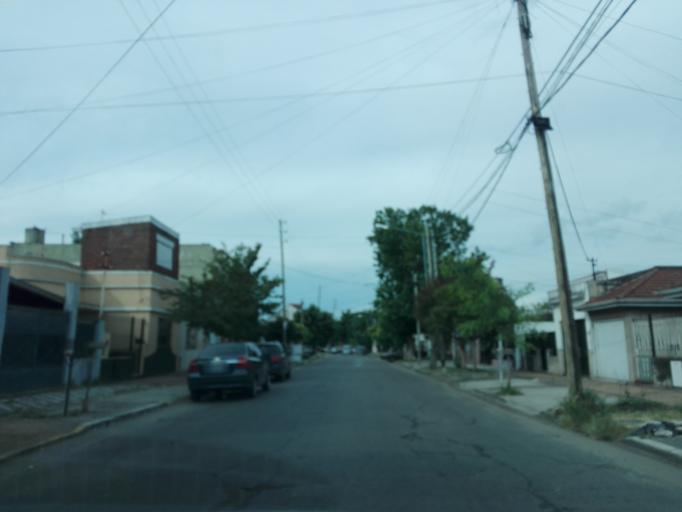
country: AR
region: Buenos Aires
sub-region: Partido de Lanus
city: Lanus
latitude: -34.7233
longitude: -58.3863
